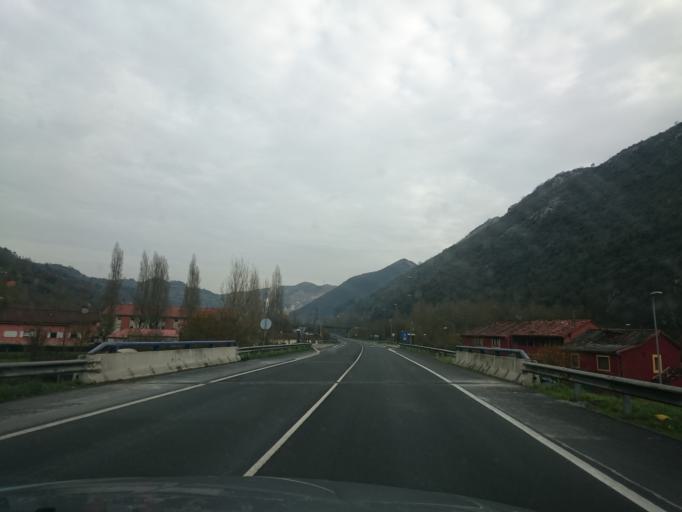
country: ES
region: Asturias
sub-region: Province of Asturias
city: Oviedo
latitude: 43.3258
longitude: -5.7885
